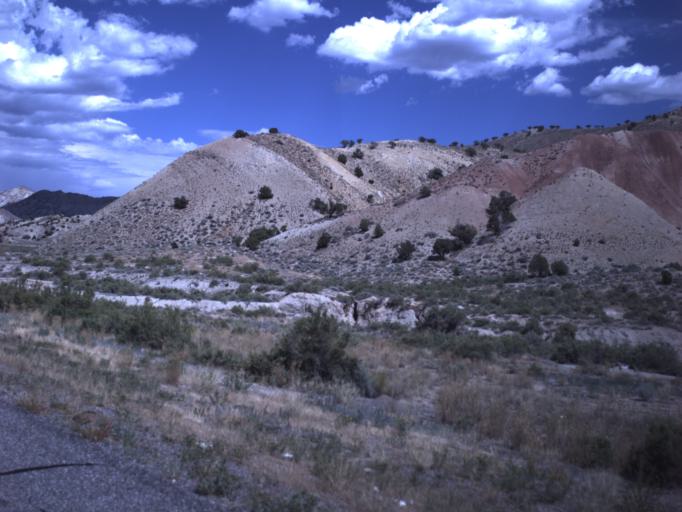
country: US
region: Utah
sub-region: Sevier County
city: Aurora
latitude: 38.8269
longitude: -111.9562
